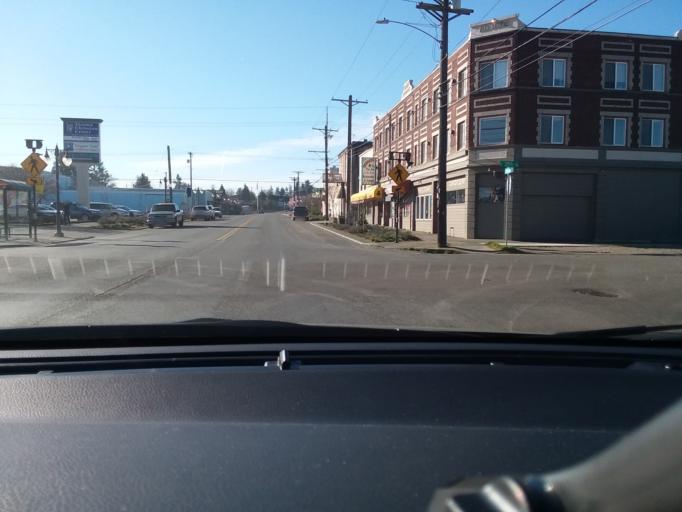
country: US
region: Washington
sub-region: Pierce County
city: Tacoma
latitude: 47.2306
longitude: -122.4212
